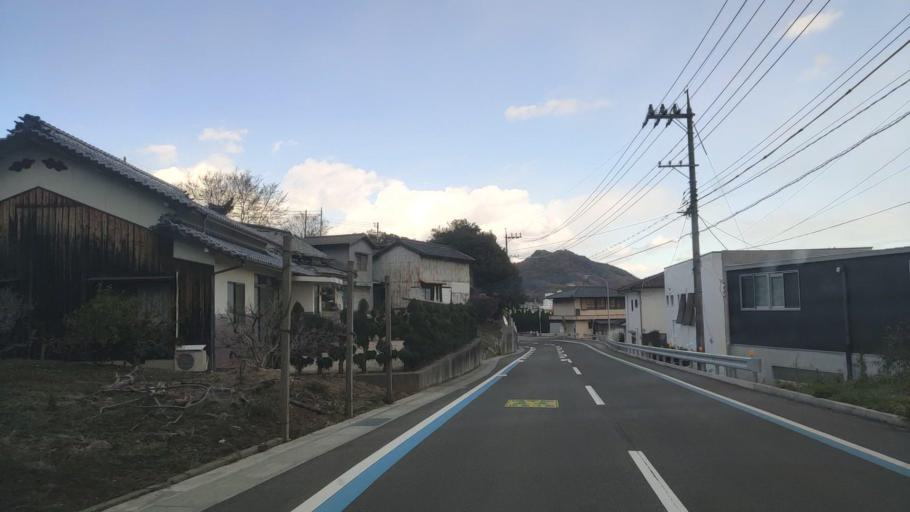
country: JP
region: Hiroshima
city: Innoshima
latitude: 34.1990
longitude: 133.0886
